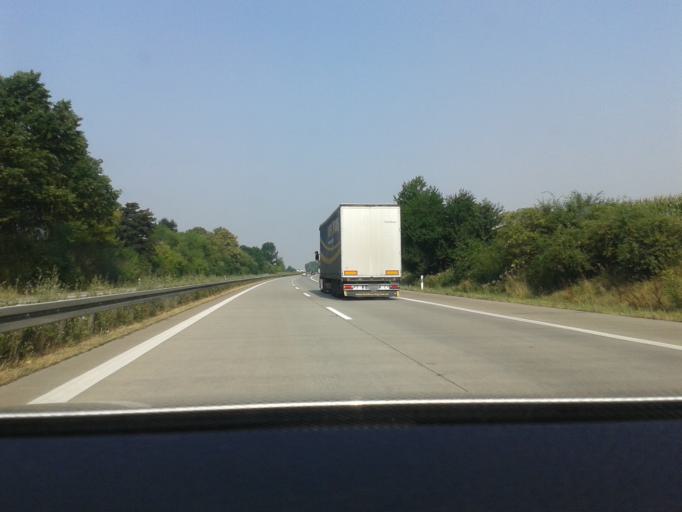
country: DE
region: Saxony
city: Nossen
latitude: 51.0737
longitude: 13.3116
